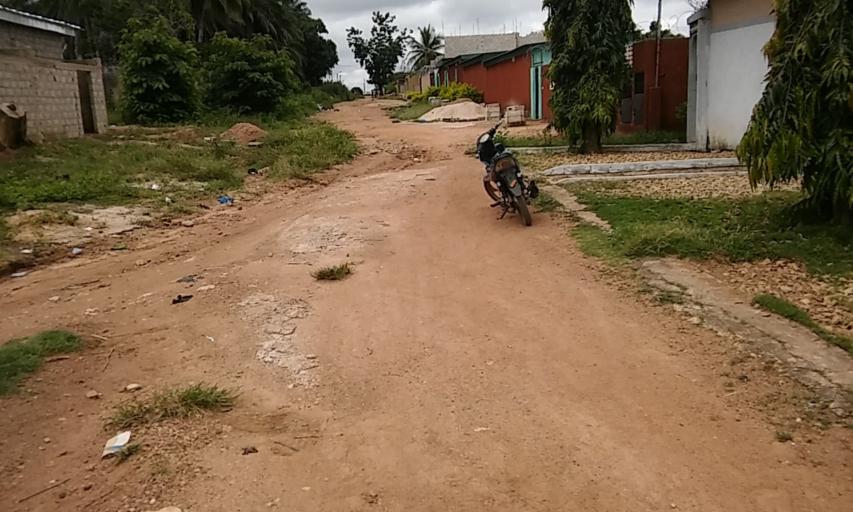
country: CI
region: Vallee du Bandama
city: Bouake
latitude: 7.6940
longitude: -5.0593
